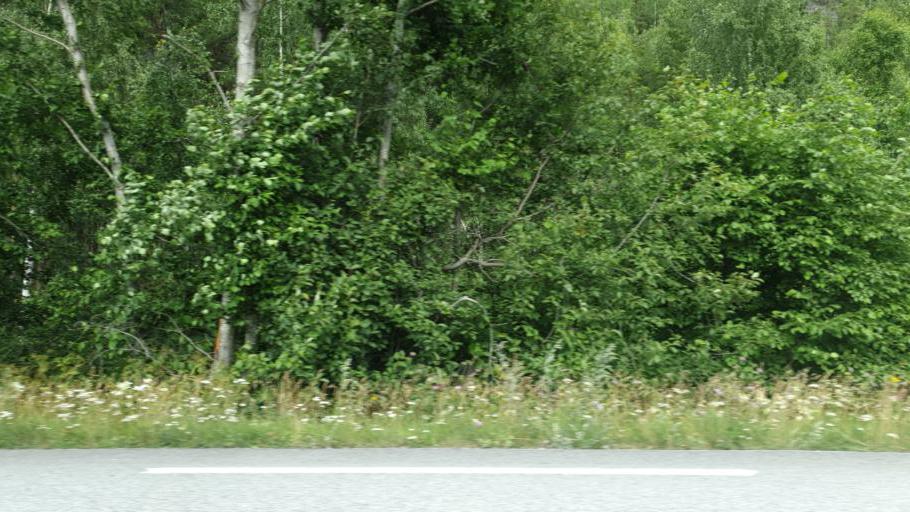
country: NO
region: Oppland
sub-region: Sel
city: Otta
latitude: 61.8436
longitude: 9.3851
